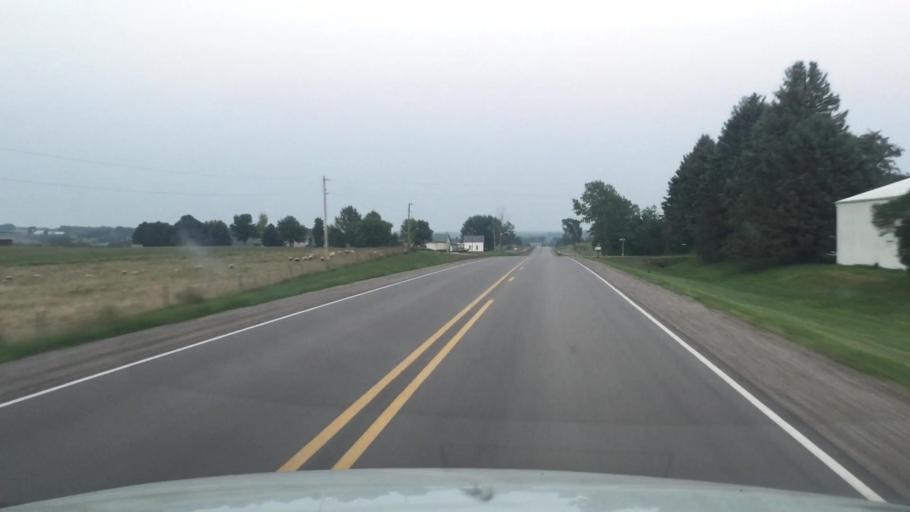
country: US
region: Iowa
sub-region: Marion County
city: Melcher-Dallas
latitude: 41.1898
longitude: -93.4061
